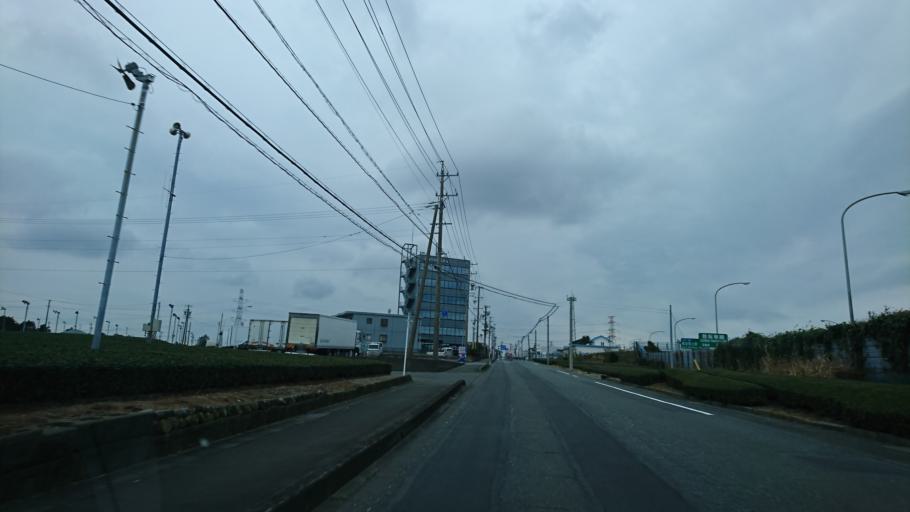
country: JP
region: Shizuoka
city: Kanaya
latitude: 34.7624
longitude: 138.1488
